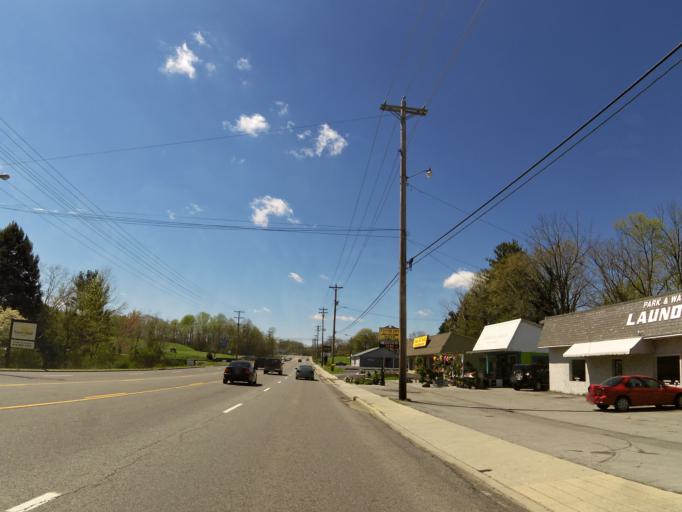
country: US
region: Tennessee
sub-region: DeKalb County
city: Smithville
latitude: 35.9584
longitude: -85.8261
